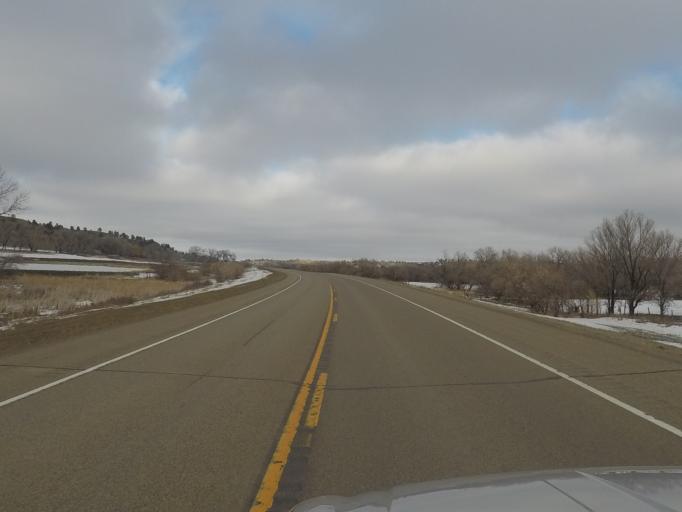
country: US
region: Montana
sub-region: Golden Valley County
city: Ryegate
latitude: 46.2967
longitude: -109.2419
